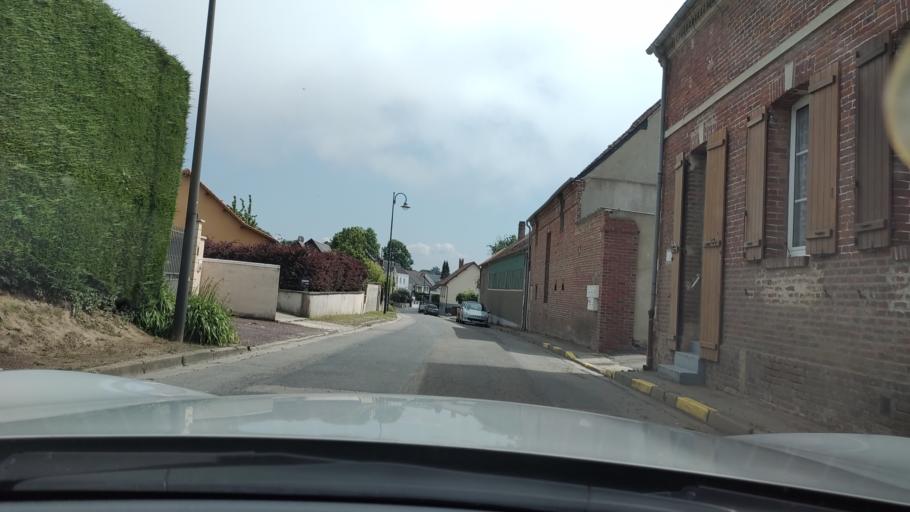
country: FR
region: Picardie
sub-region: Departement de la Somme
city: Ault
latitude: 50.0760
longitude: 1.4573
